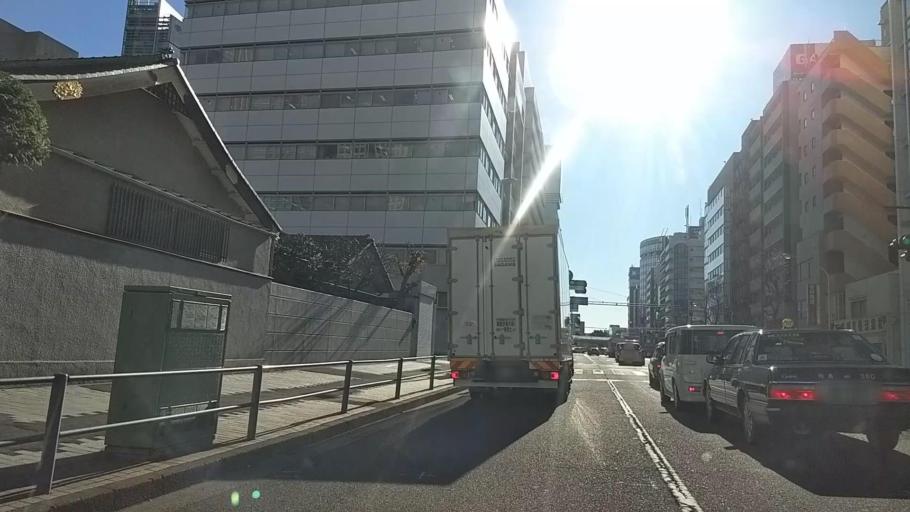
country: JP
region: Kanagawa
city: Yokohama
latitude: 35.4514
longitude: 139.6294
